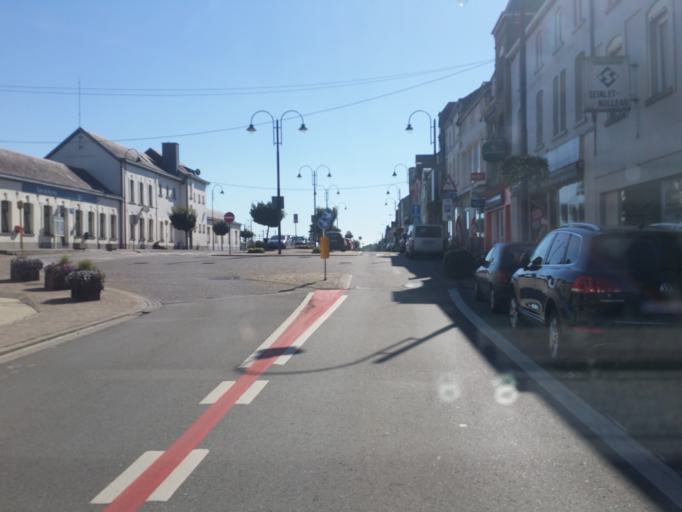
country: BE
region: Wallonia
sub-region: Province du Luxembourg
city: Bertrix
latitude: 49.8534
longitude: 5.2667
